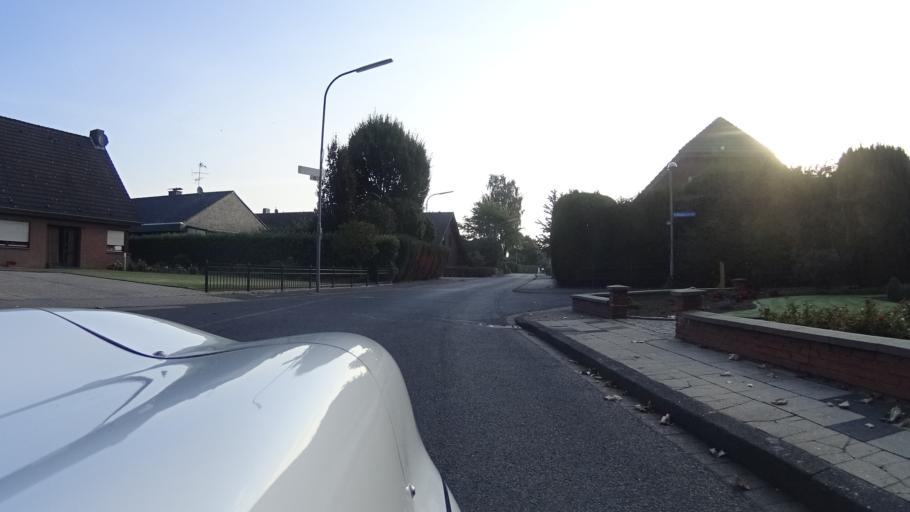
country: NL
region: Limburg
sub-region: Gemeente Venlo
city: Arcen
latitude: 51.4962
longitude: 6.2327
